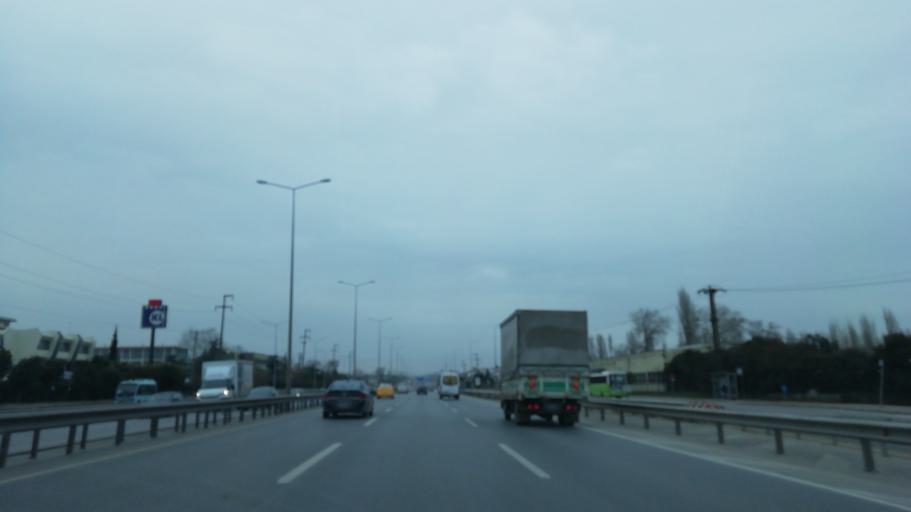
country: TR
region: Kocaeli
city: Darica
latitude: 40.8098
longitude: 29.3706
